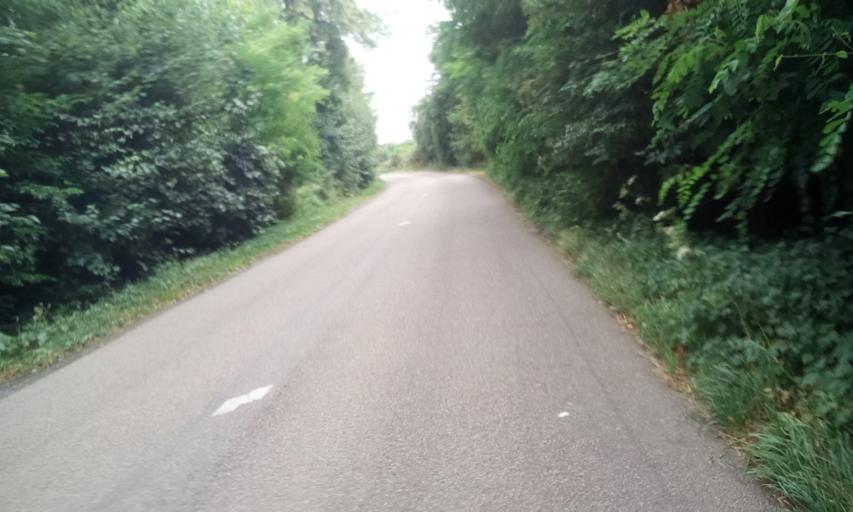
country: FR
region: Lower Normandy
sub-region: Departement du Calvados
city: Bavent
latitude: 49.2093
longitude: -0.1787
